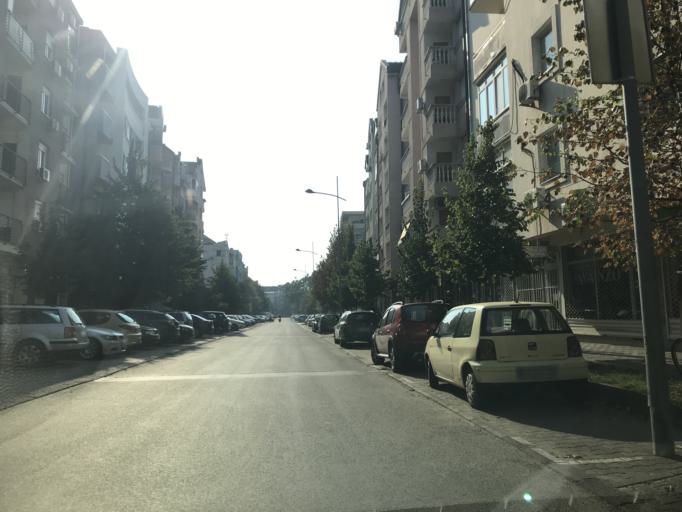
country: RS
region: Autonomna Pokrajina Vojvodina
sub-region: Juznobacki Okrug
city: Novi Sad
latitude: 45.2529
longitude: 19.8352
